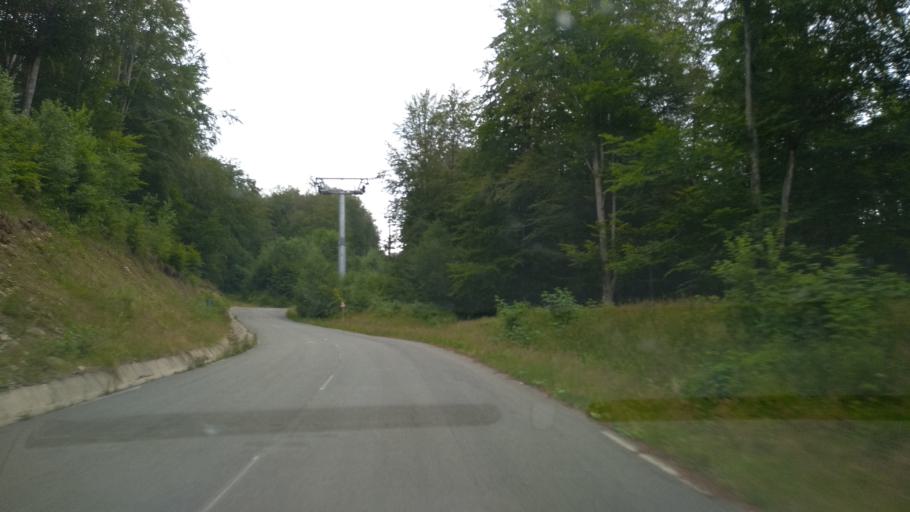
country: RO
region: Hunedoara
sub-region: Municipiul  Vulcan
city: Jiu-Paroseni
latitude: 45.3391
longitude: 23.2909
